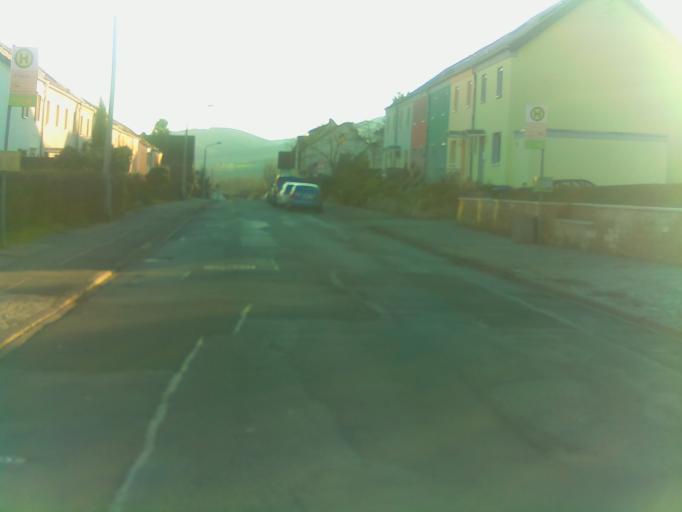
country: DE
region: Thuringia
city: Rudolstadt
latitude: 50.6935
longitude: 11.3235
